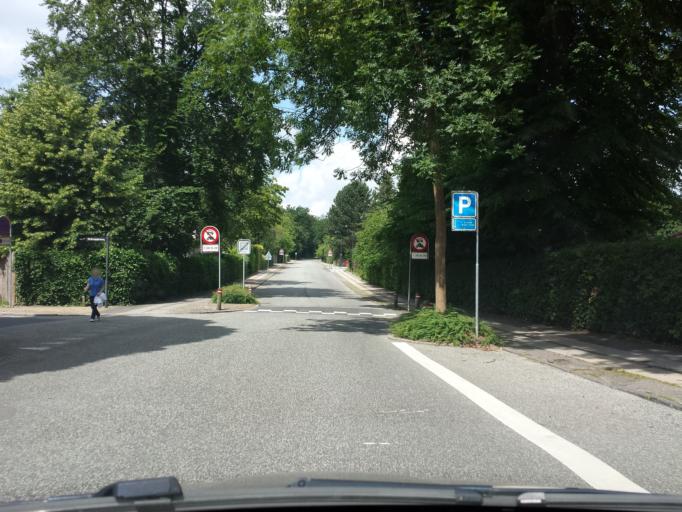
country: DK
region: Capital Region
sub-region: Gentofte Kommune
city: Charlottenlund
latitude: 55.7664
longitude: 12.5680
